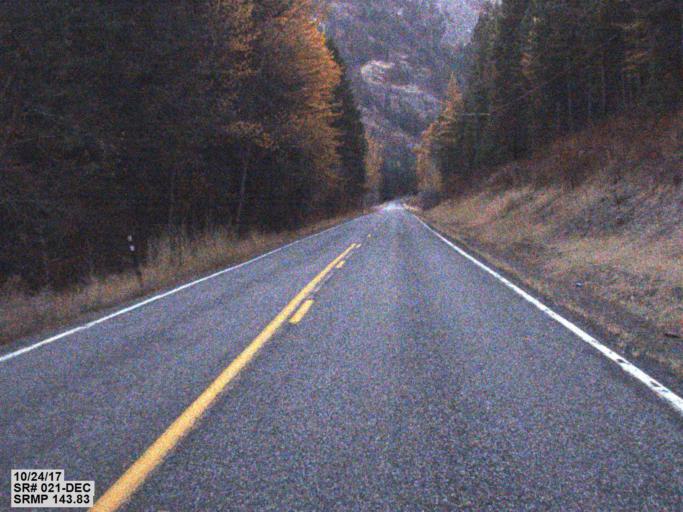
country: US
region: Washington
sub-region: Ferry County
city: Republic
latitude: 48.4351
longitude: -118.7354
